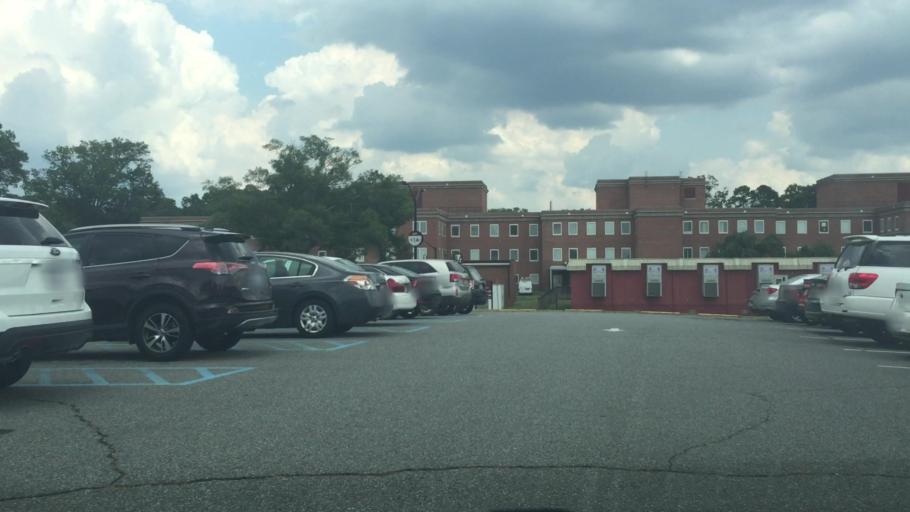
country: US
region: North Carolina
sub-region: Rowan County
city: Salisbury
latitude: 35.6819
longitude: -80.4893
